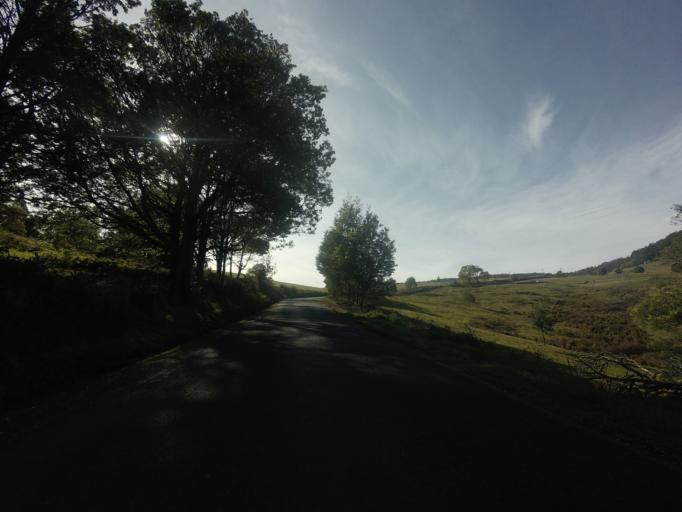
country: AU
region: Tasmania
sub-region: Kingborough
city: Kettering
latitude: -43.1715
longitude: 147.1676
